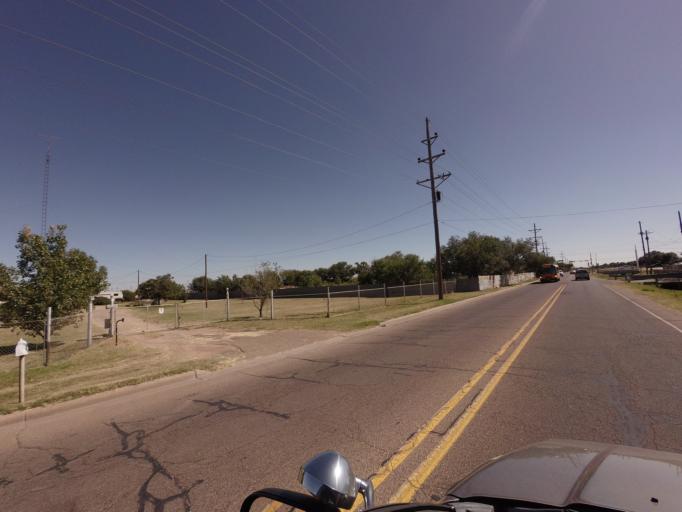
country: US
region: New Mexico
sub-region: Curry County
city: Clovis
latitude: 34.4062
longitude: -103.2317
